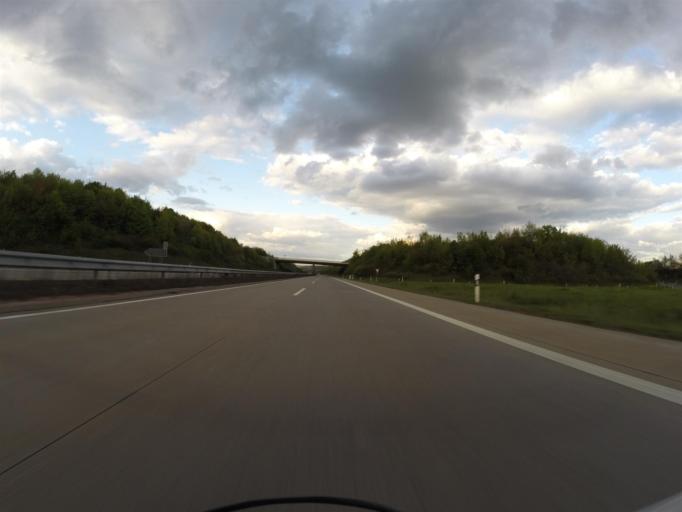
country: DE
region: Rheinland-Pfalz
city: Dreisen
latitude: 49.6070
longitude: 8.0021
